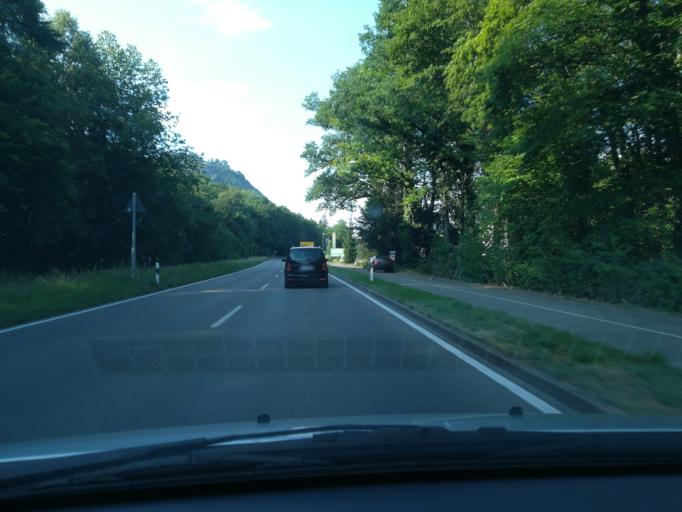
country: DE
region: Baden-Wuerttemberg
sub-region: Freiburg Region
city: Singen
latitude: 47.7514
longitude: 8.8173
